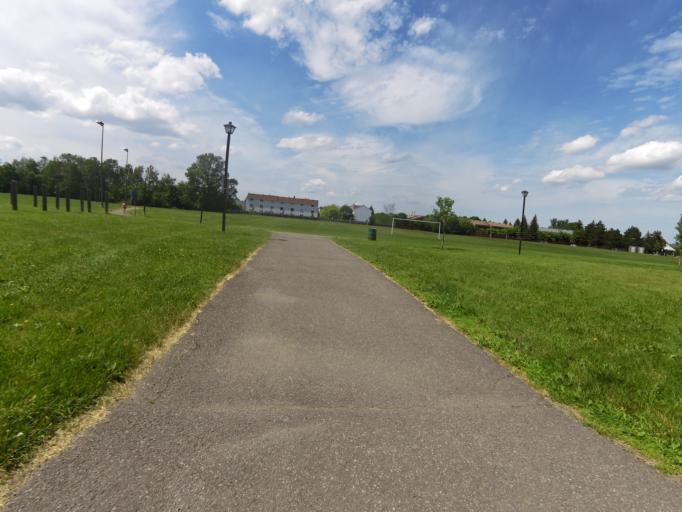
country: CA
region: Ontario
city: Ottawa
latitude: 45.3618
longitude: -75.6371
